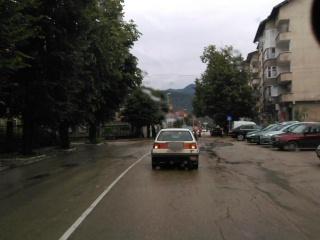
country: BG
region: Lovech
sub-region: Obshtina Troyan
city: Troyan
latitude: 42.8724
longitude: 24.7130
